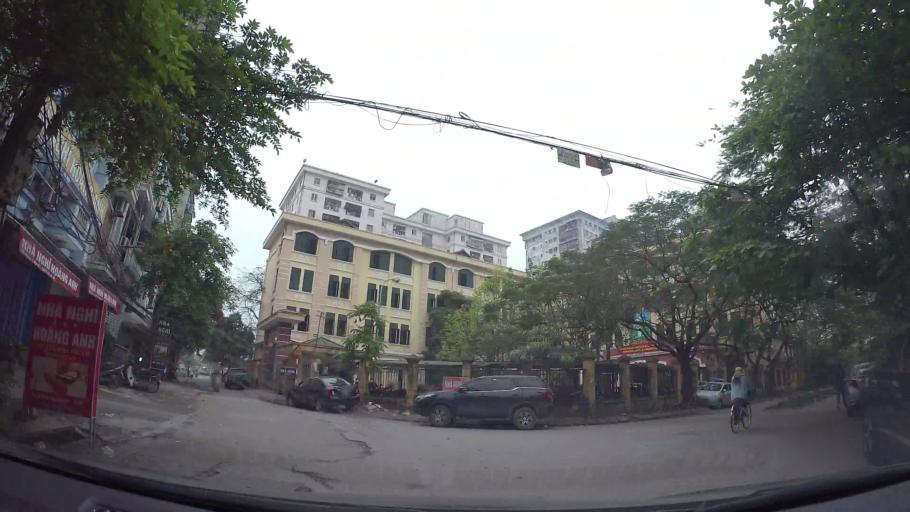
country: VN
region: Ha Noi
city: Hai BaTrung
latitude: 20.9847
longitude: 105.8595
